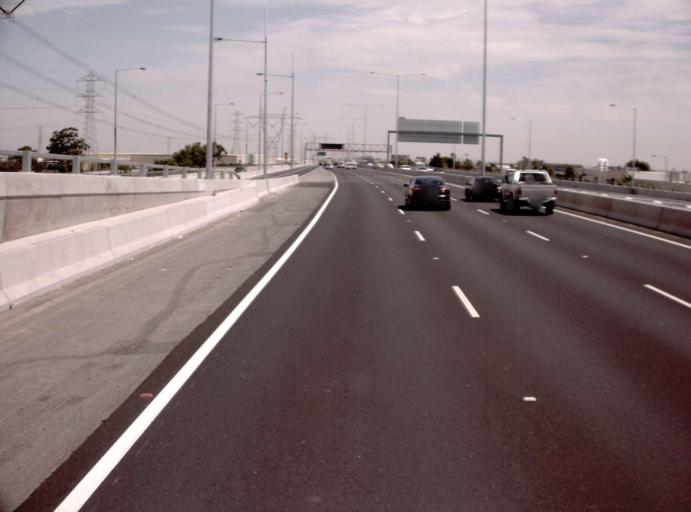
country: AU
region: Victoria
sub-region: Moreland
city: Gowanbrae
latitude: -37.7055
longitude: 144.8884
